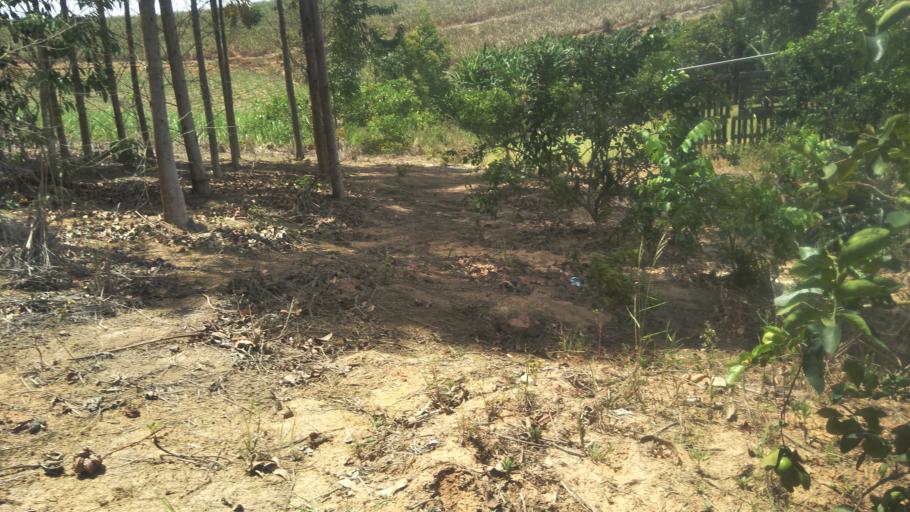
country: BR
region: Pernambuco
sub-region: Vitoria De Santo Antao
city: Vitoria de Santo Antao
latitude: -8.1522
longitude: -35.2483
